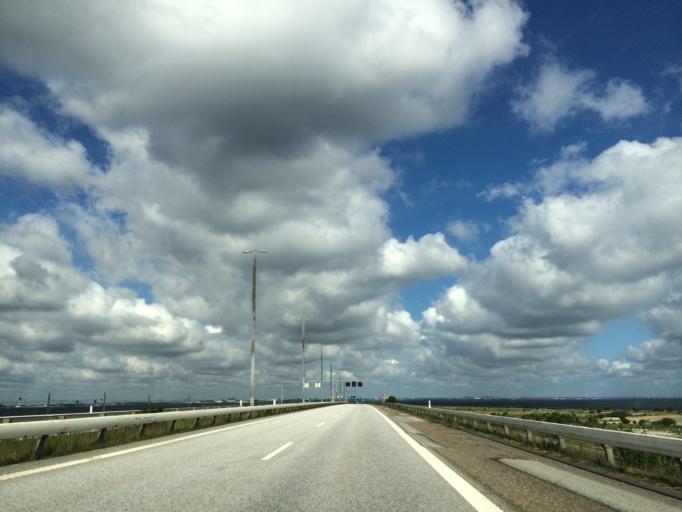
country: DK
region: Capital Region
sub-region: Dragor Kommune
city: Dragor
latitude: 55.6034
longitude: 12.7446
